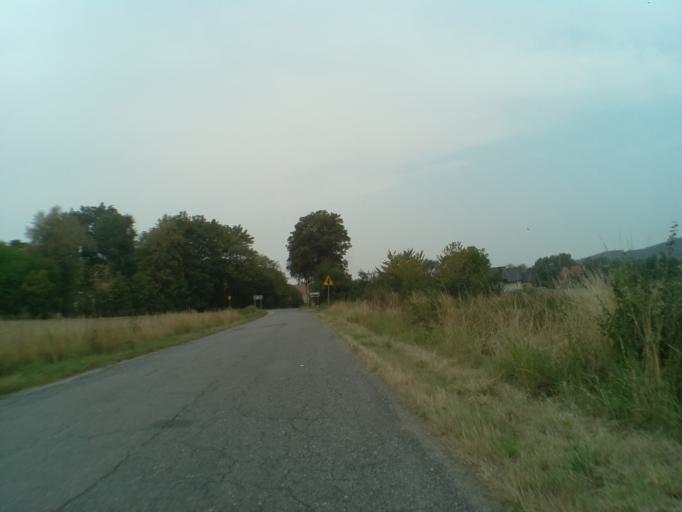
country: PL
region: Lower Silesian Voivodeship
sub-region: Powiat swidnicki
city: Strzegom
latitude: 50.9752
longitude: 16.3081
